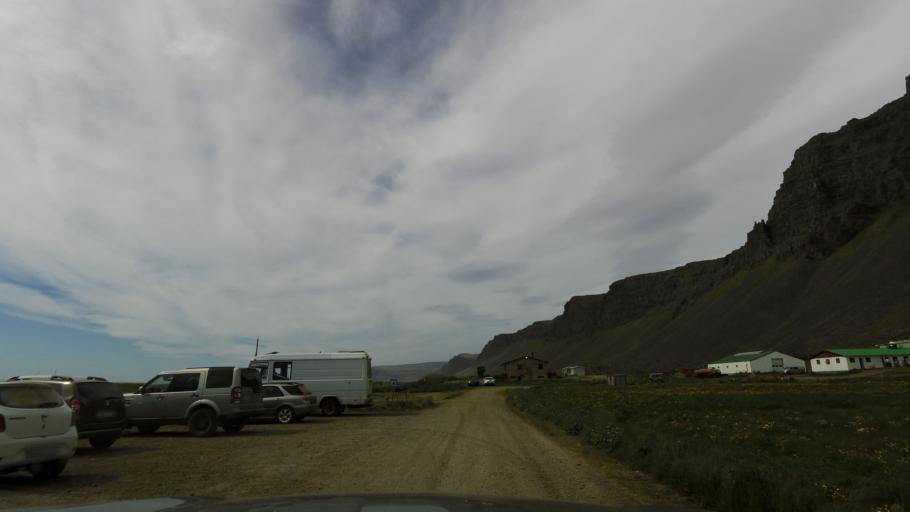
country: IS
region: West
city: Olafsvik
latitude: 65.4925
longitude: -24.0904
